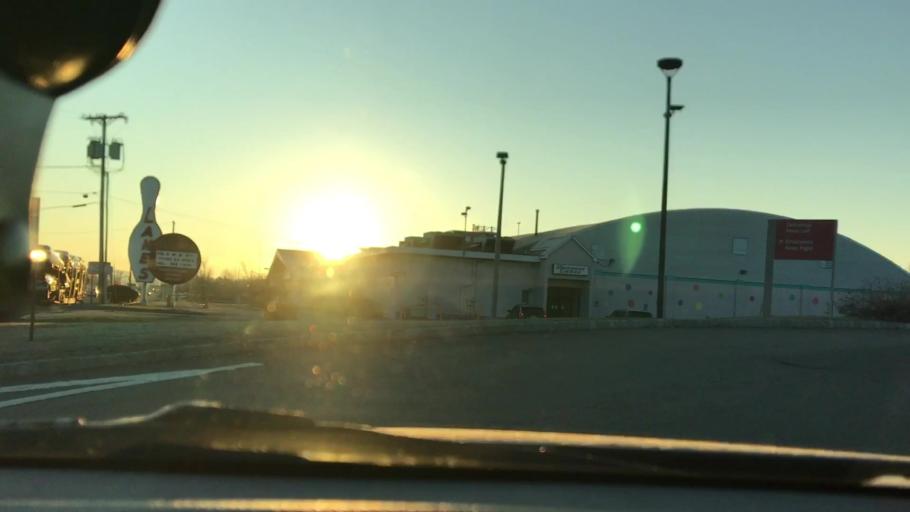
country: US
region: New Jersey
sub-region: Morris County
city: Hanover
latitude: 40.8104
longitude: -74.3840
